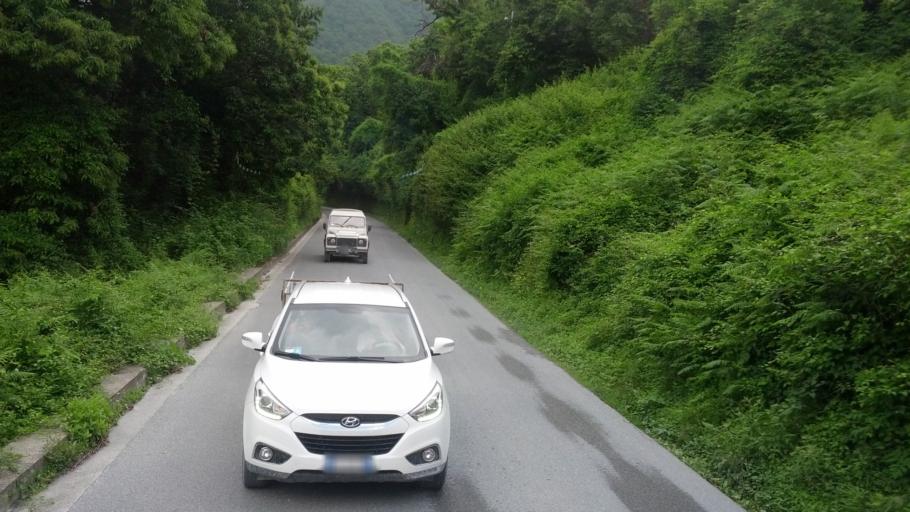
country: IT
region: Tuscany
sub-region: Provincia di Massa-Carrara
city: Massa
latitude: 44.0792
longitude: 10.1261
